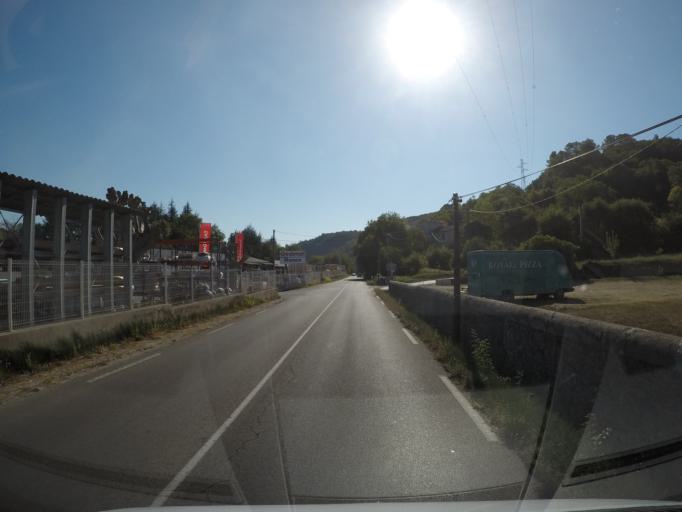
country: FR
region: Languedoc-Roussillon
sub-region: Departement du Gard
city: Anduze
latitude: 44.0407
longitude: 3.9858
